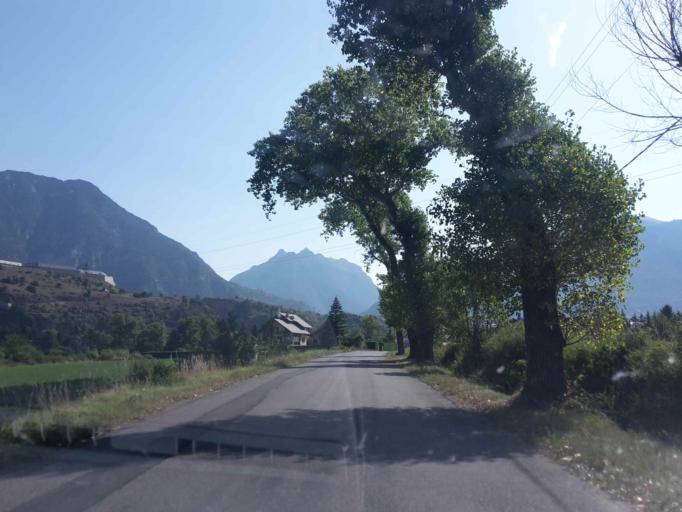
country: FR
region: Provence-Alpes-Cote d'Azur
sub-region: Departement des Hautes-Alpes
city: Guillestre
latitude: 44.6608
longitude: 6.6136
